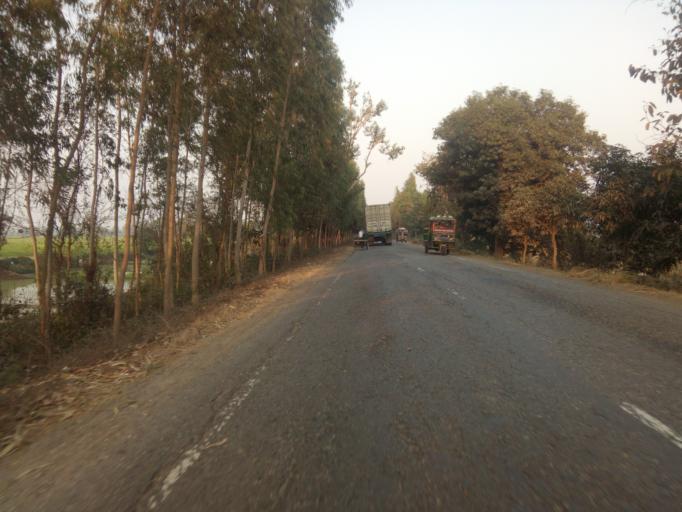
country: BD
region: Rajshahi
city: Bogra
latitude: 24.5579
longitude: 89.1993
